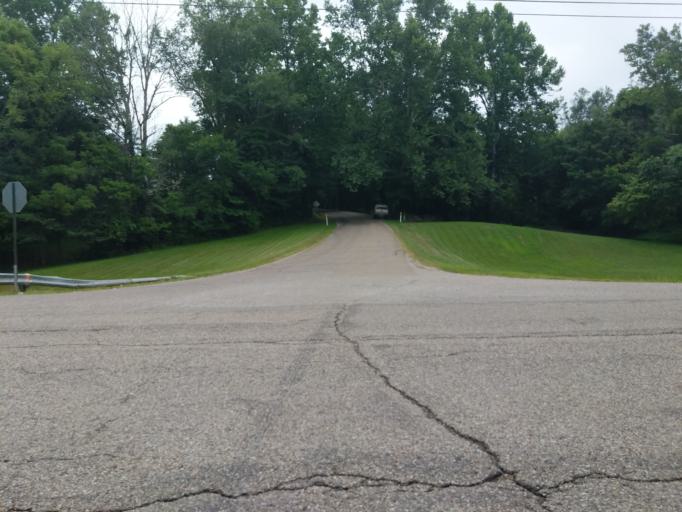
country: US
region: Ohio
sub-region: Athens County
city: The Plains
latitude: 39.3770
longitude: -82.1420
